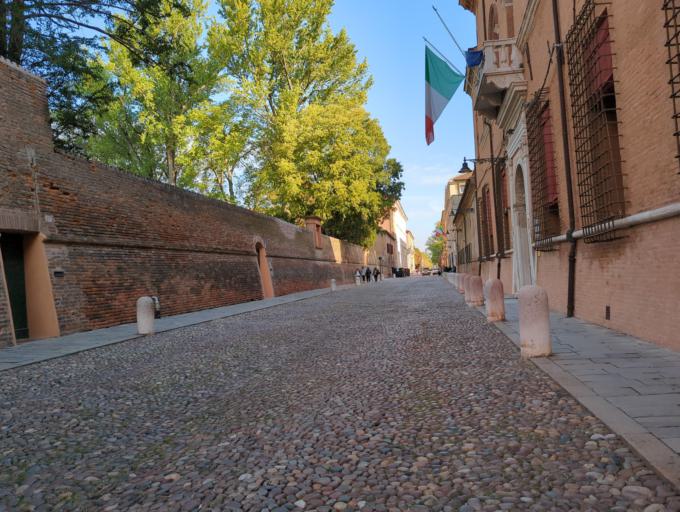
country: IT
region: Emilia-Romagna
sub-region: Provincia di Ferrara
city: Ferrara
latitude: 44.8407
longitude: 11.6208
